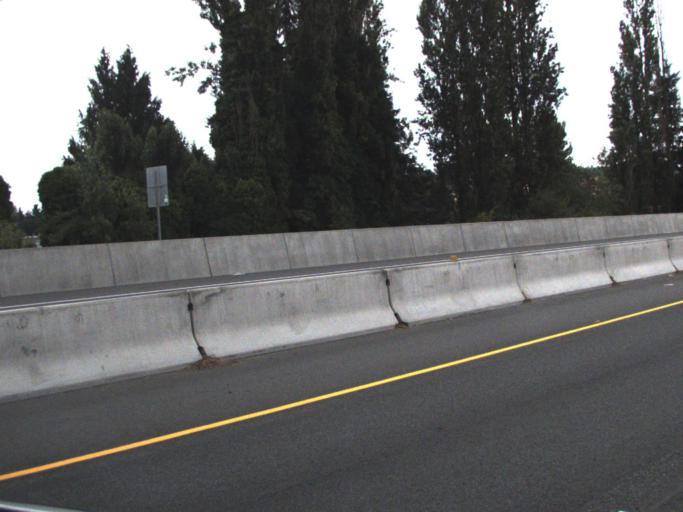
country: US
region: Washington
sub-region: Snohomish County
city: Monroe
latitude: 47.8531
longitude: -121.9981
